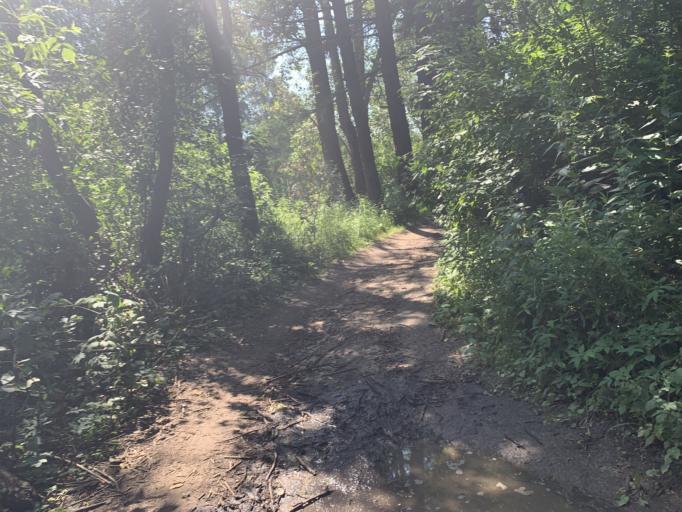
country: RU
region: Moskovskaya
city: Mamontovka
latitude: 55.9695
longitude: 37.8153
